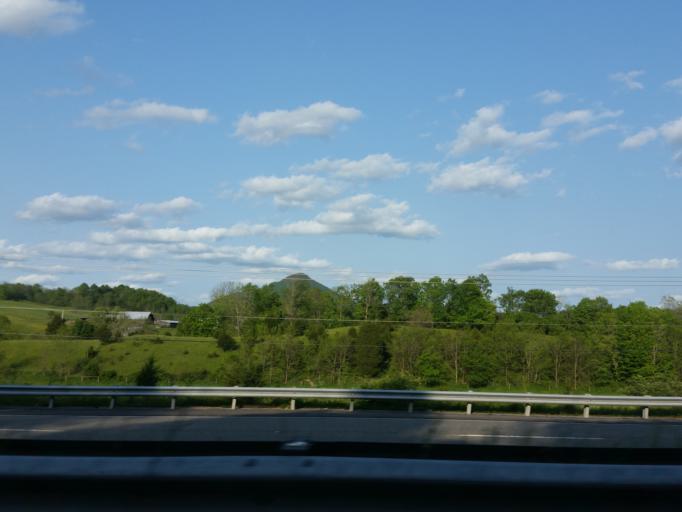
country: US
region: Virginia
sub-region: Tazewell County
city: Claypool Hill
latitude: 37.0317
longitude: -81.7984
